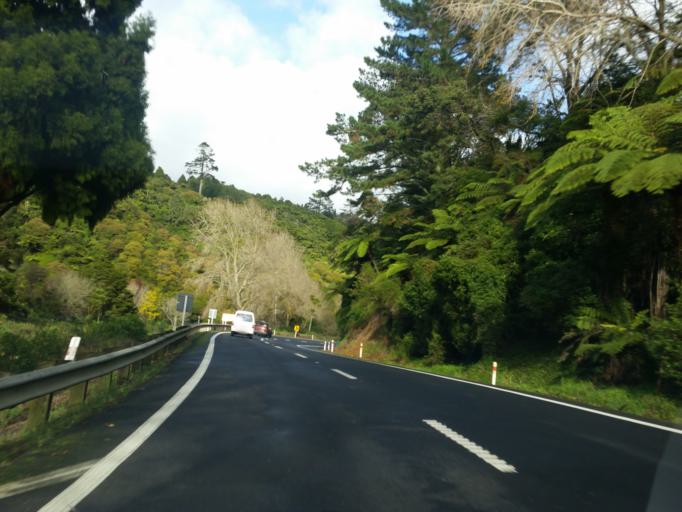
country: NZ
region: Waikato
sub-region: Hauraki District
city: Waihi
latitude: -37.4183
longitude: 175.7533
